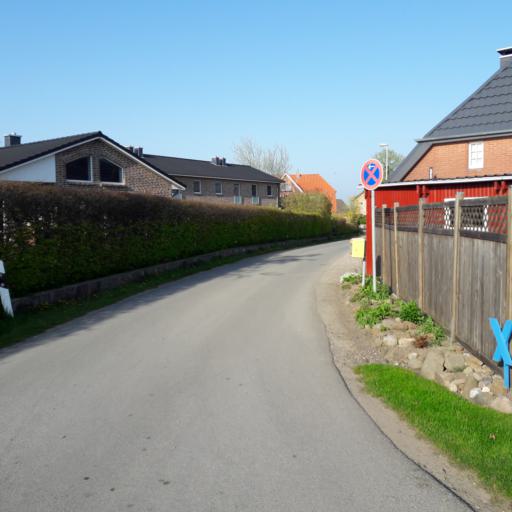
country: DE
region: Schleswig-Holstein
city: Burg auf Fehmarn
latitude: 54.4265
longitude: 11.2261
